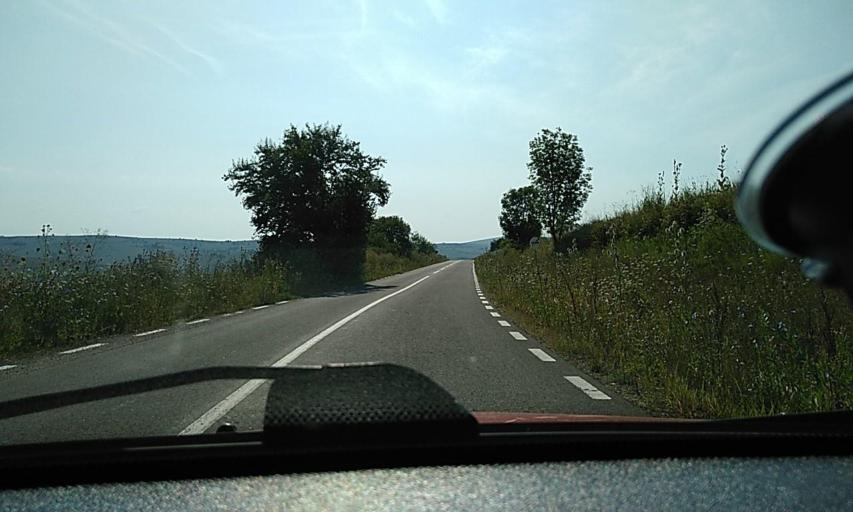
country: RO
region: Brasov
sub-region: Comuna Bunesti
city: Bunesti
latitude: 46.0628
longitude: 25.0846
